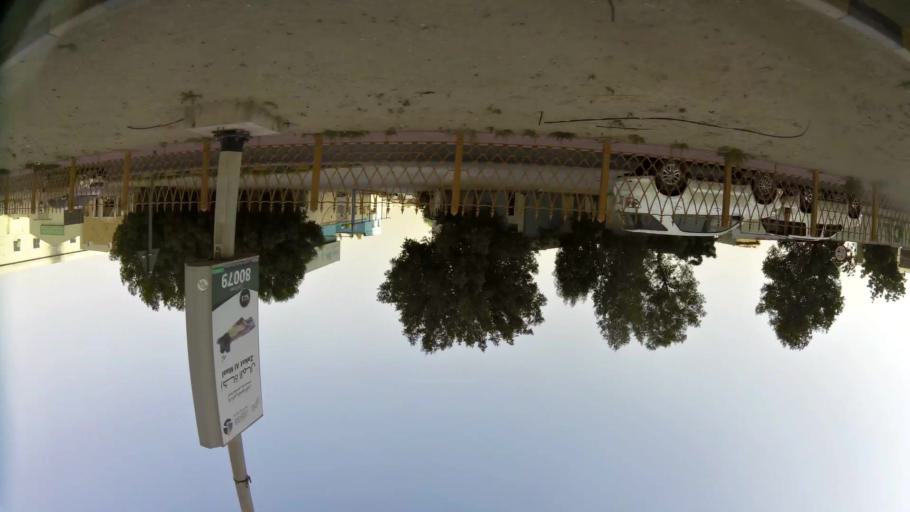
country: AE
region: Ajman
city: Ajman
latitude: 25.3962
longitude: 55.4553
